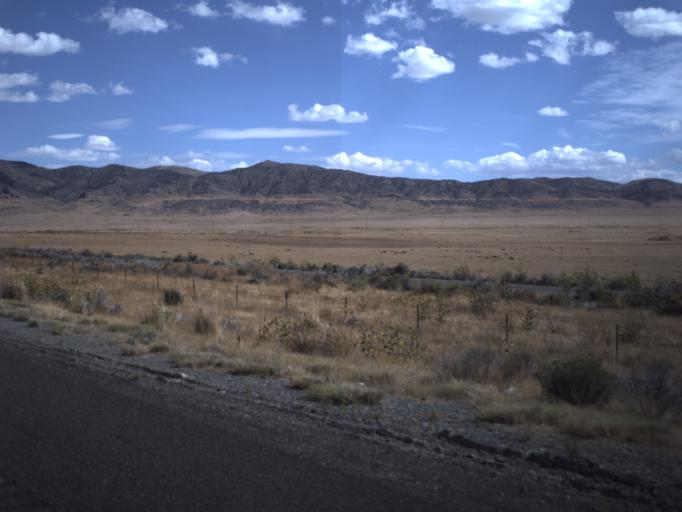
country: US
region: Utah
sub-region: Tooele County
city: Grantsville
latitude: 40.7638
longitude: -112.9962
